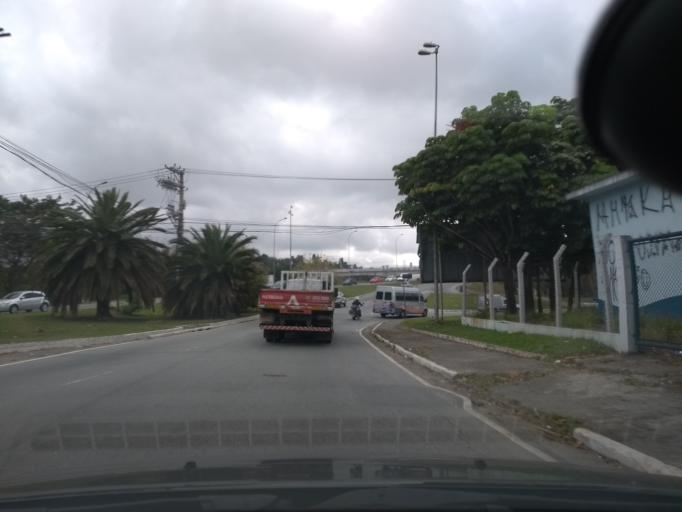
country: BR
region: Sao Paulo
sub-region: Guarulhos
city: Guarulhos
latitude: -23.4584
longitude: -46.4934
